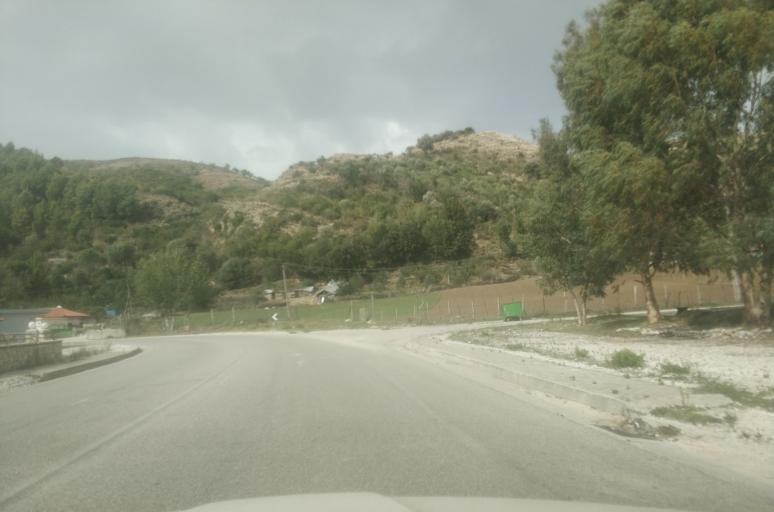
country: AL
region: Gjirokaster
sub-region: Rrethi i Tepelenes
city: Memaliaj
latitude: 40.3528
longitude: 19.9719
